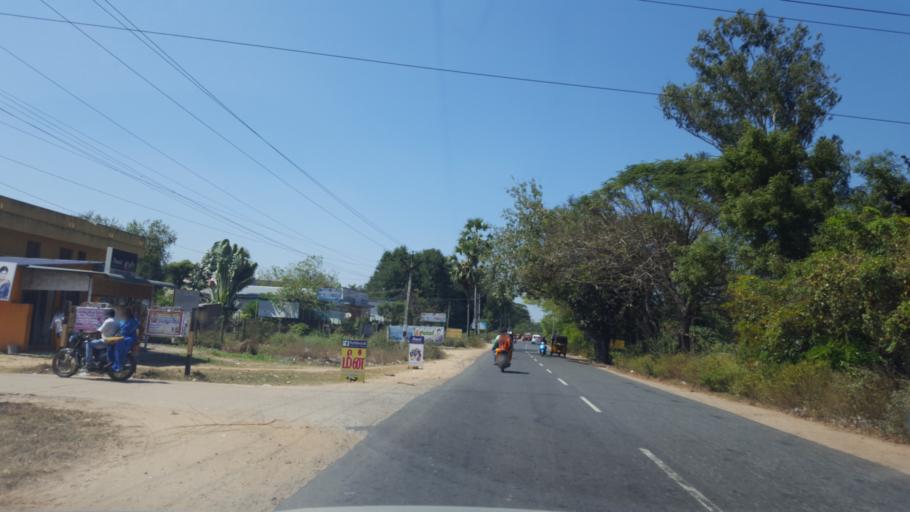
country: IN
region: Tamil Nadu
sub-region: Kancheepuram
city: Chengalpattu
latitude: 12.7206
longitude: 79.9543
